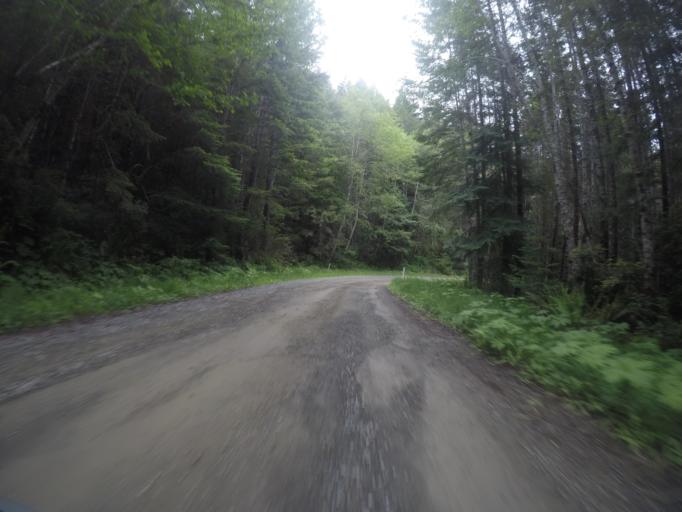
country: US
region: California
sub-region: Humboldt County
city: Westhaven-Moonstone
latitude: 41.2350
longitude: -123.9913
